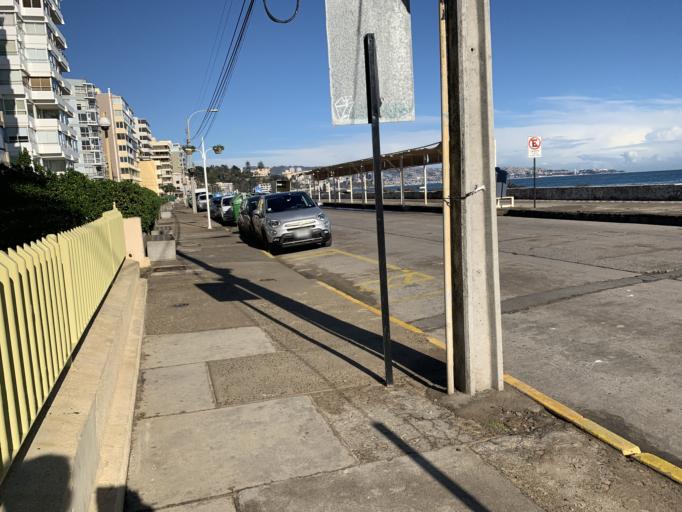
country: CL
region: Valparaiso
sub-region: Provincia de Valparaiso
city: Vina del Mar
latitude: -33.0145
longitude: -71.5566
